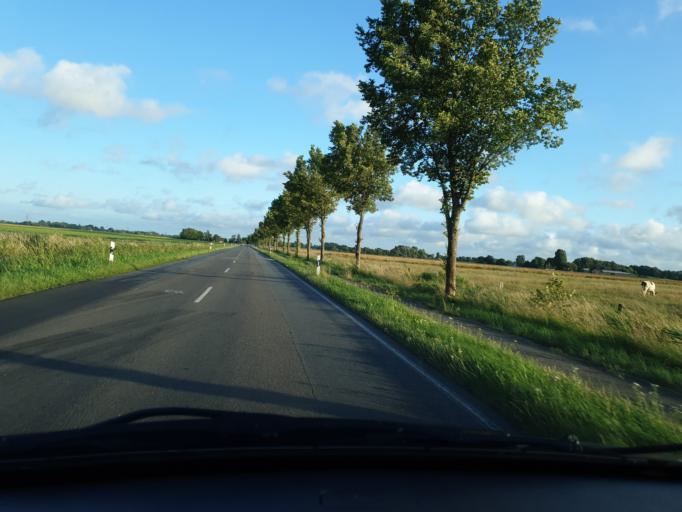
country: DE
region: Schleswig-Holstein
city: Epenwohrden
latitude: 54.1282
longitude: 9.0169
